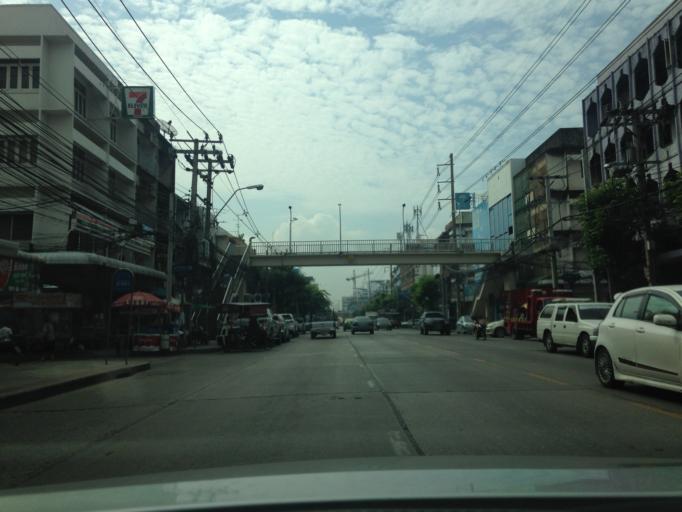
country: TH
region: Bangkok
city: Bang Sue
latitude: 13.8044
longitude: 100.5215
